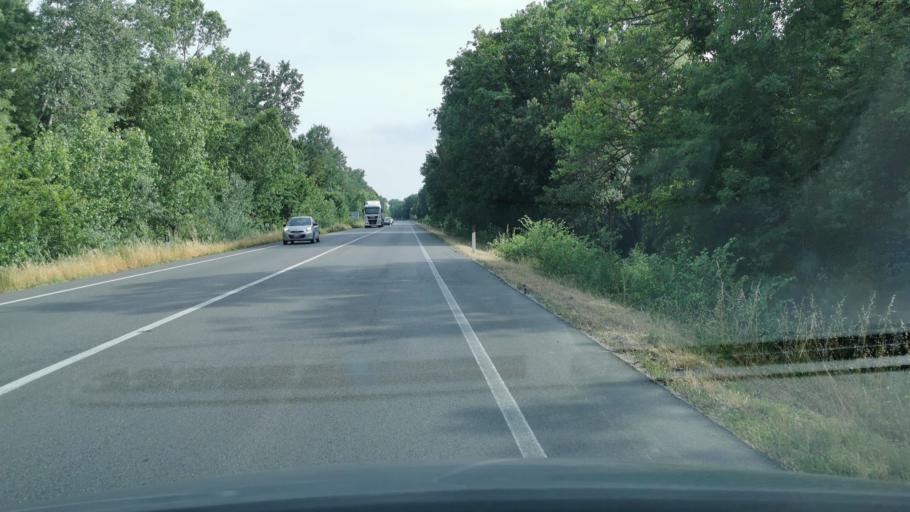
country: IT
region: Emilia-Romagna
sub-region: Provincia di Ravenna
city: Marina Romea
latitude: 44.4932
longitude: 12.2155
